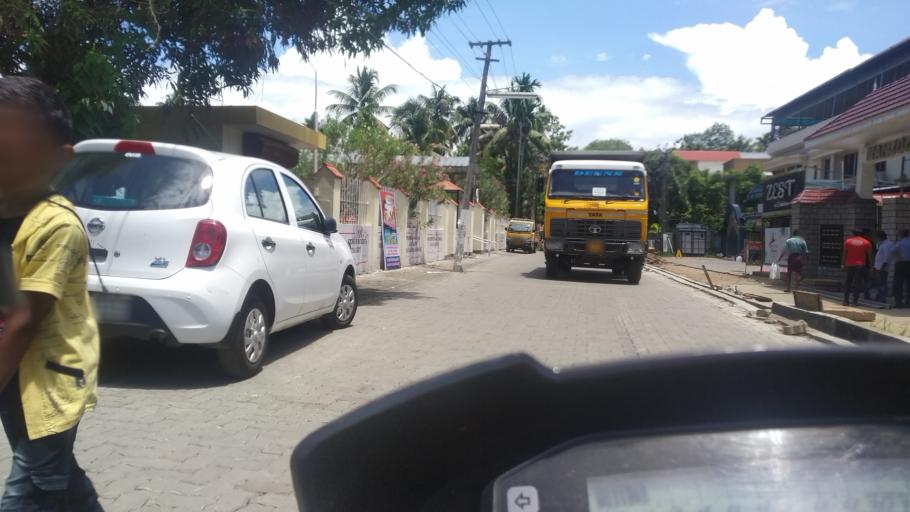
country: IN
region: Kerala
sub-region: Ernakulam
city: Elur
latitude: 10.0476
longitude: 76.2187
